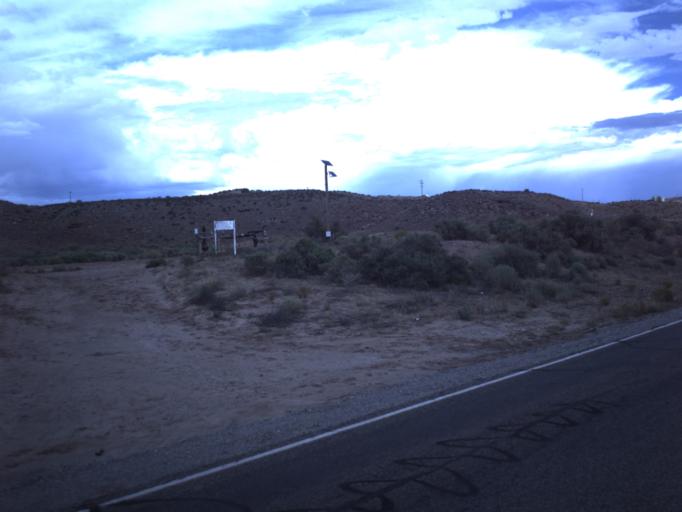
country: US
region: Utah
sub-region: San Juan County
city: Blanding
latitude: 37.2348
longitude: -109.2225
